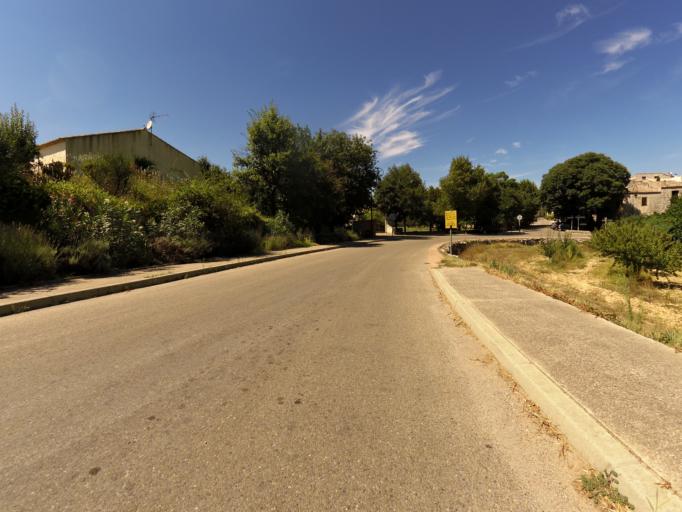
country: FR
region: Languedoc-Roussillon
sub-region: Departement du Gard
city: Sommieres
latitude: 43.8350
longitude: 4.0635
